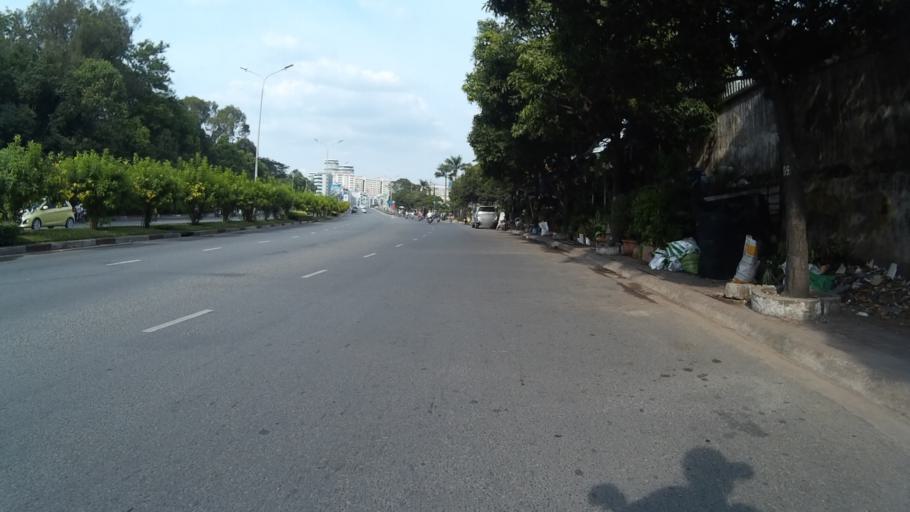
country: VN
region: Ho Chi Minh City
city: Quan Mot
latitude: 10.7848
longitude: 106.7083
